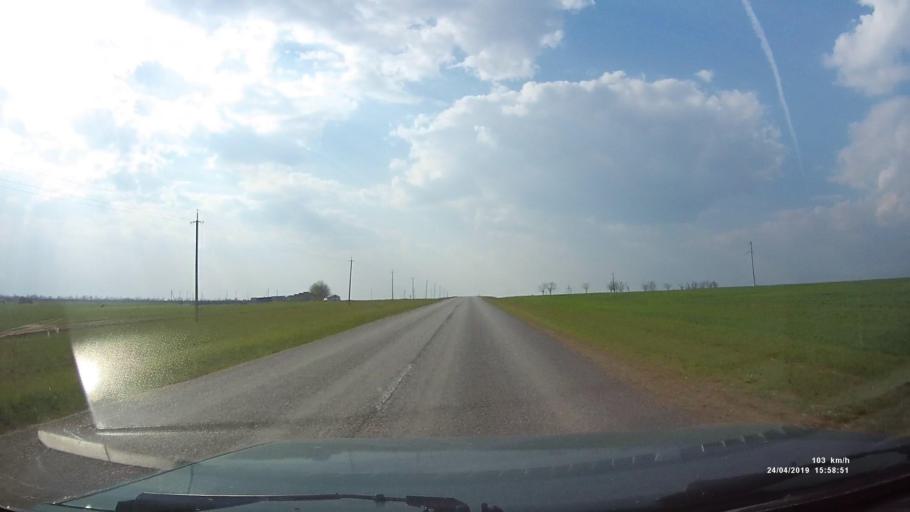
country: RU
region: Kalmykiya
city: Yashalta
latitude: 46.6176
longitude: 42.4839
